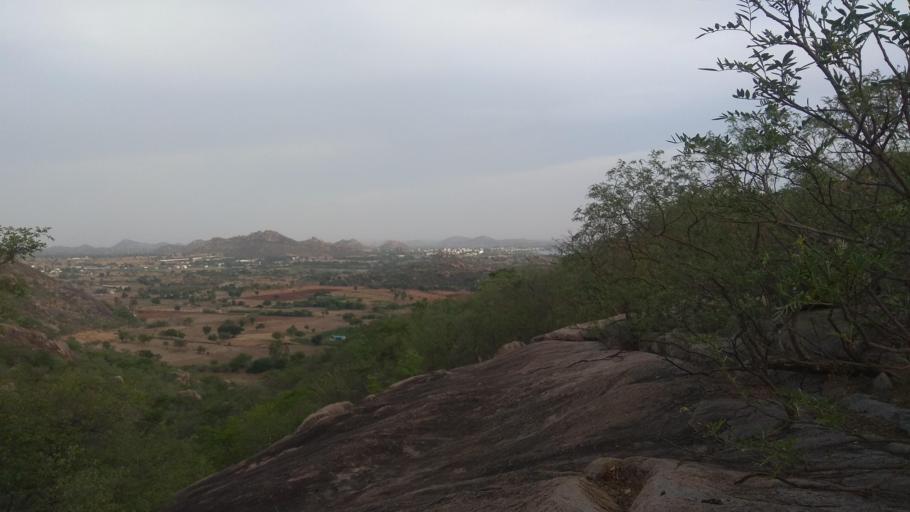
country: IN
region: Telangana
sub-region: Mahbubnagar
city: Farrukhnagar
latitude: 16.8911
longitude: 78.5082
